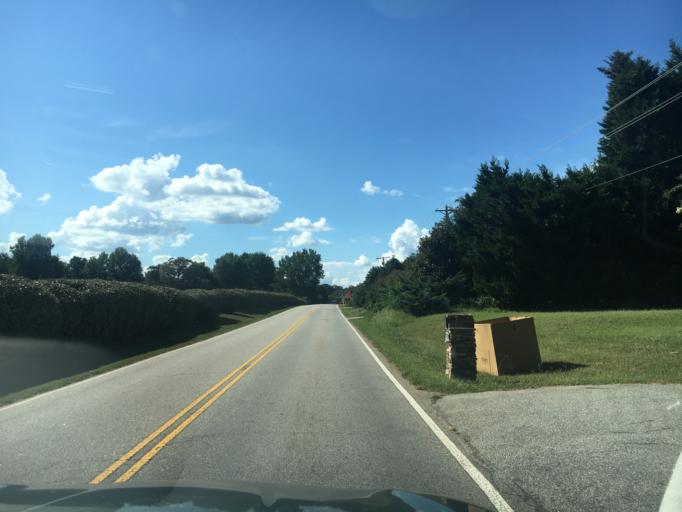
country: US
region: South Carolina
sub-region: Greenville County
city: Five Forks
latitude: 34.8275
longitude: -82.2443
